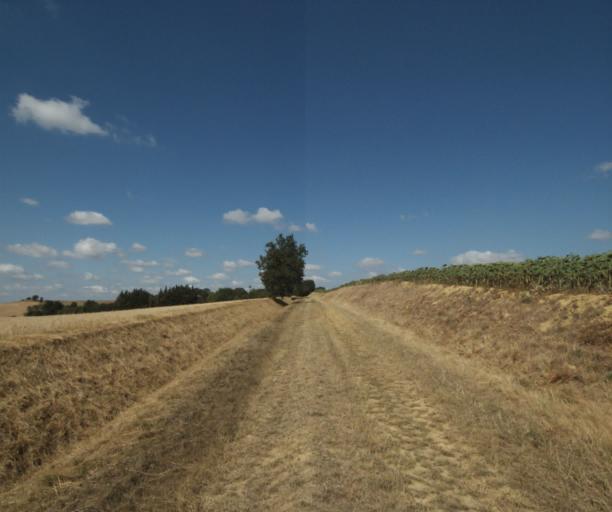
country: FR
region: Midi-Pyrenees
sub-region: Departement de la Haute-Garonne
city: Auriac-sur-Vendinelle
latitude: 43.4684
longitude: 1.7883
